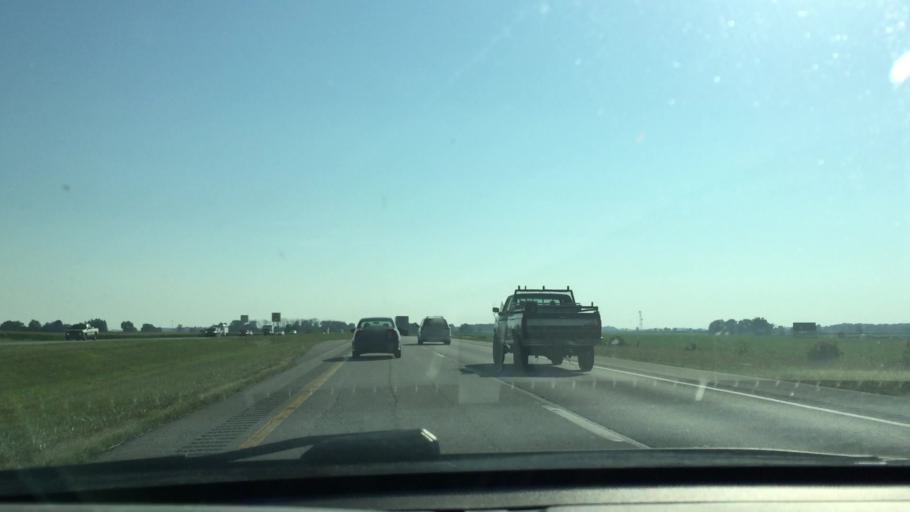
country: US
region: Ohio
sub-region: Greene County
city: Shawnee Hills
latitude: 39.5424
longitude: -83.7649
